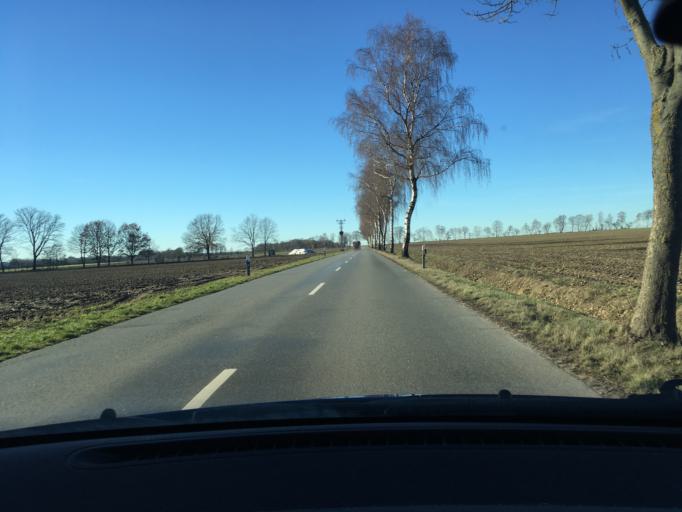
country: DE
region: Lower Saxony
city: Hanstedt Eins
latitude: 53.0222
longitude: 10.3796
